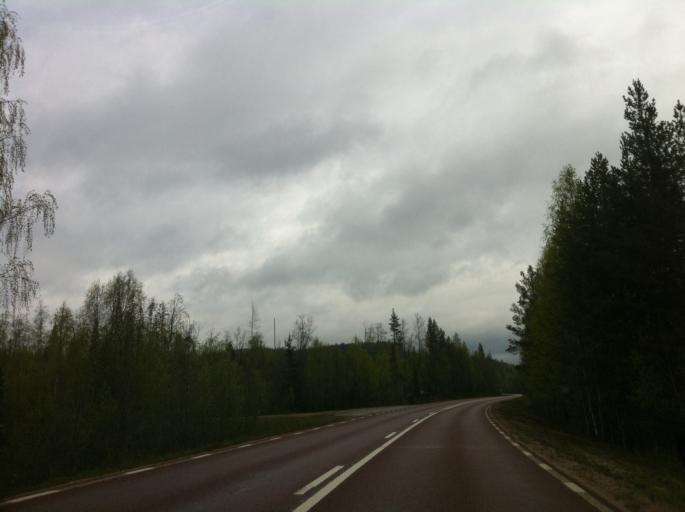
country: SE
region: Jaemtland
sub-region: Harjedalens Kommun
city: Sveg
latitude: 61.8692
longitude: 14.6330
